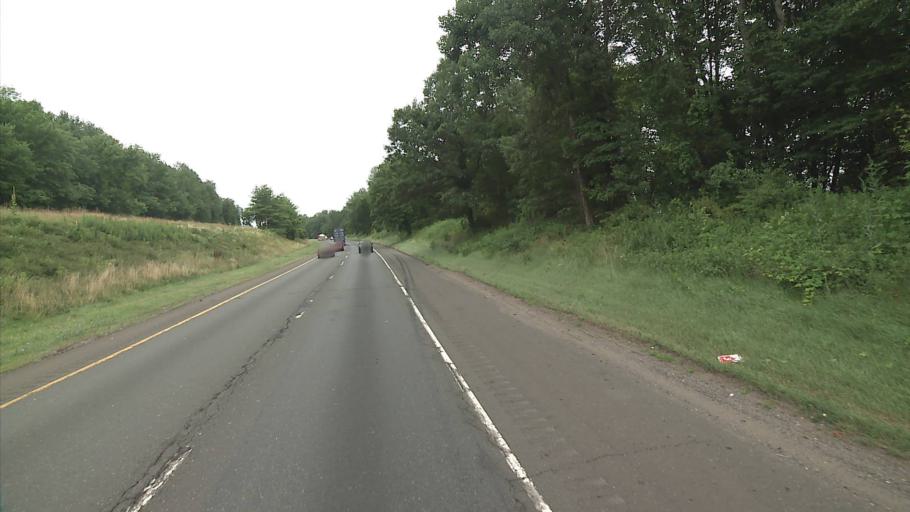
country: US
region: Connecticut
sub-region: Fairfield County
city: Newtown
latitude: 41.4270
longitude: -73.3316
